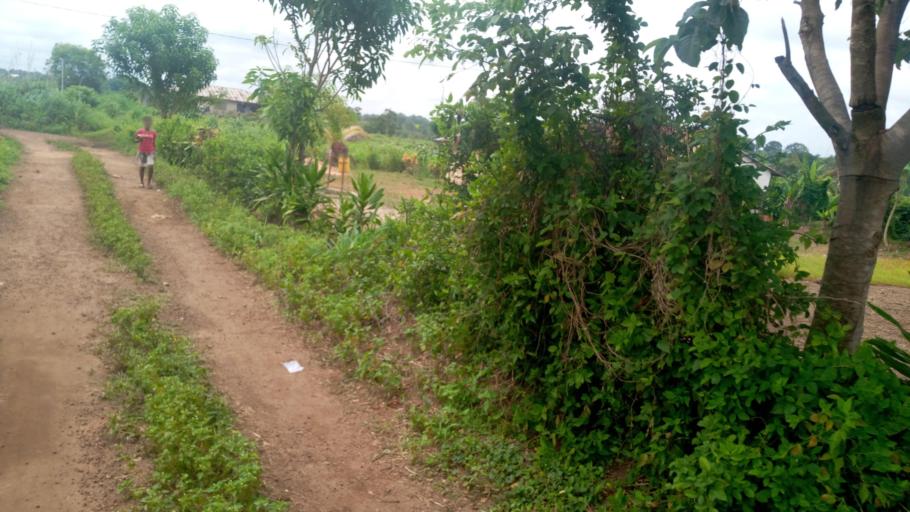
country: SL
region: Southern Province
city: Mogbwemo
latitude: 7.7740
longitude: -12.3006
